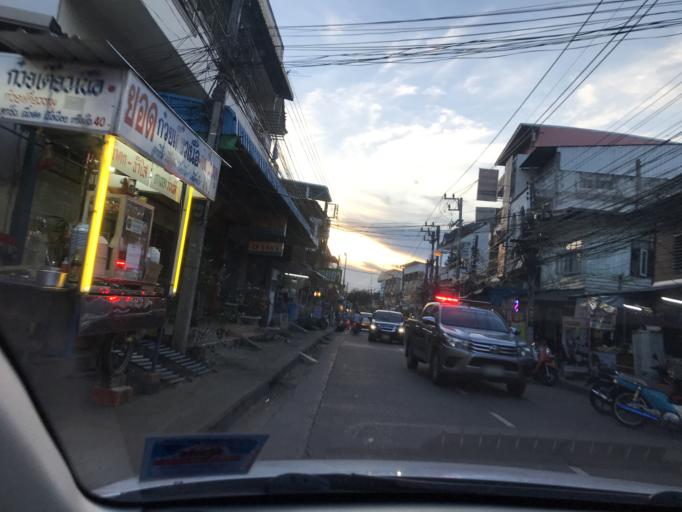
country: TH
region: Changwat Udon Thani
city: Udon Thani
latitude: 17.3947
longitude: 102.7926
